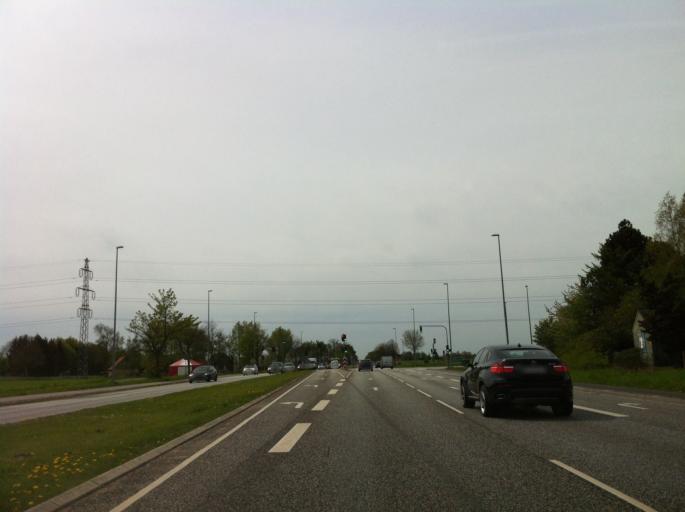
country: DK
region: Zealand
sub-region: Roskilde Kommune
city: Roskilde
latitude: 55.6234
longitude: 12.0581
